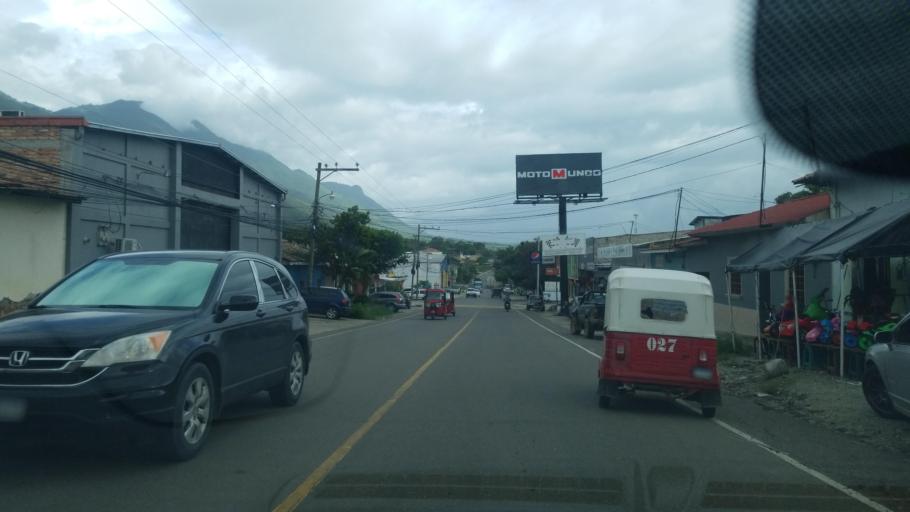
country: HN
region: Ocotepeque
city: Nueva Ocotepeque
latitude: 14.4324
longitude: -89.1828
